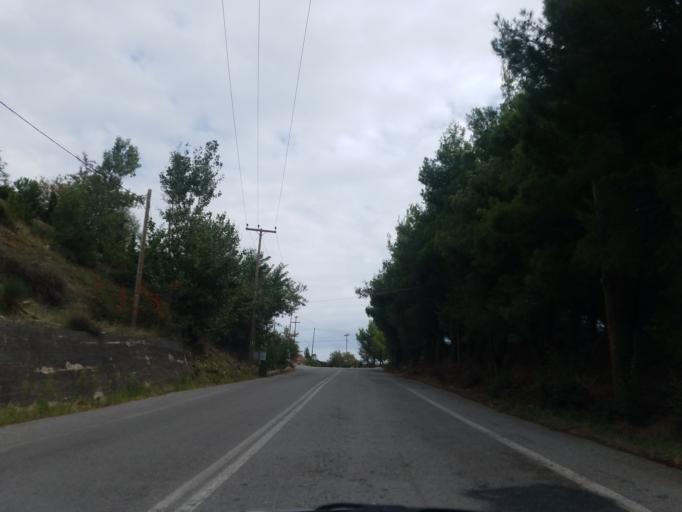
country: GR
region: Central Greece
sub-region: Nomos Voiotias
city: Arachova
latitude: 38.4840
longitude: 22.5717
